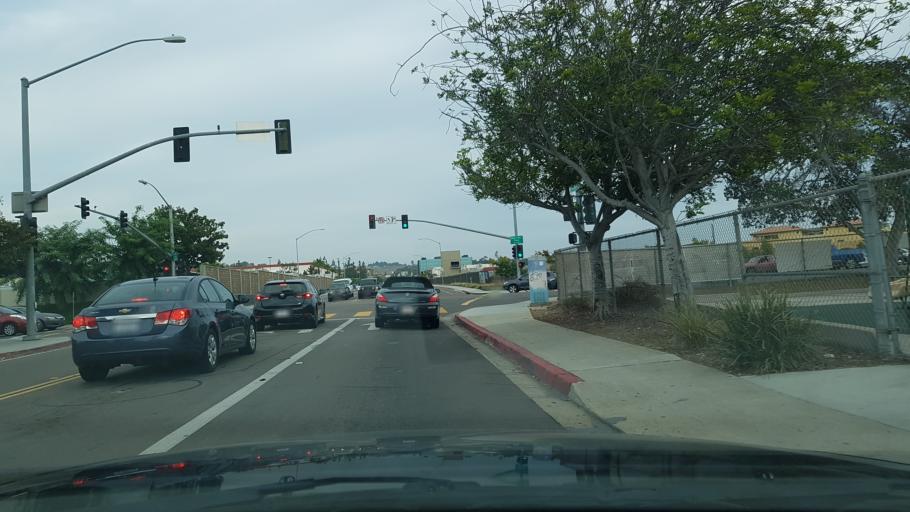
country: US
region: California
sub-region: San Diego County
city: Poway
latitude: 32.9129
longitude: -117.1249
